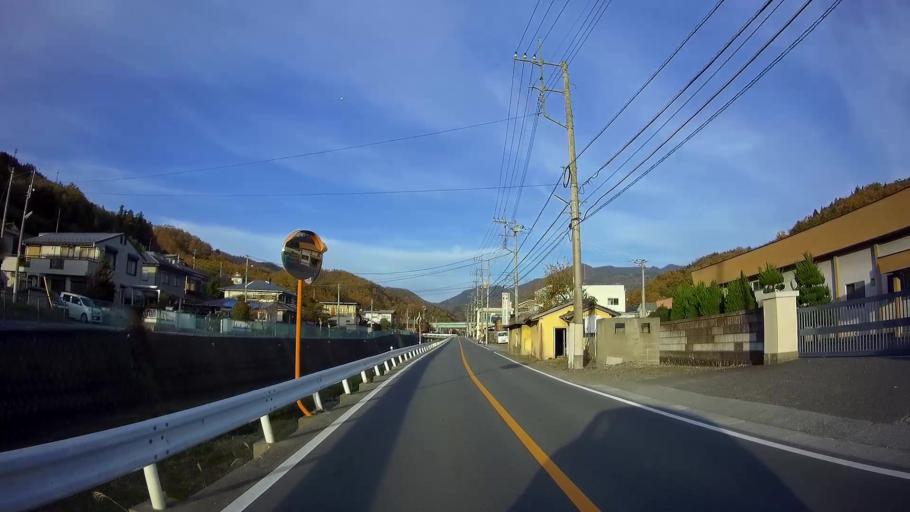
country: JP
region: Yamanashi
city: Ryuo
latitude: 35.4991
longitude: 138.4655
